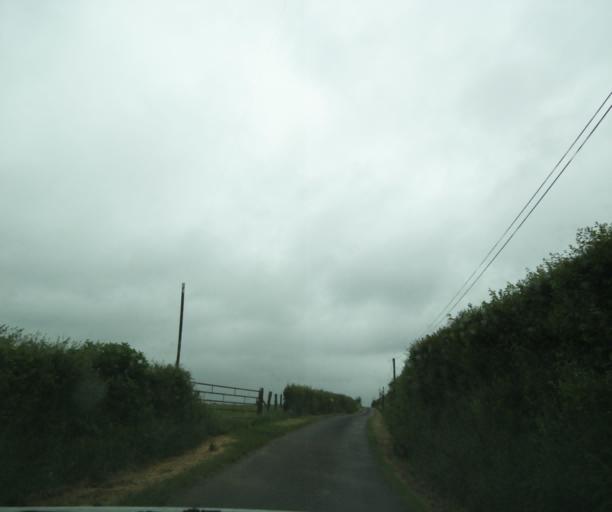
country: FR
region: Bourgogne
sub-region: Departement de Saone-et-Loire
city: Palinges
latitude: 46.4854
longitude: 4.1992
